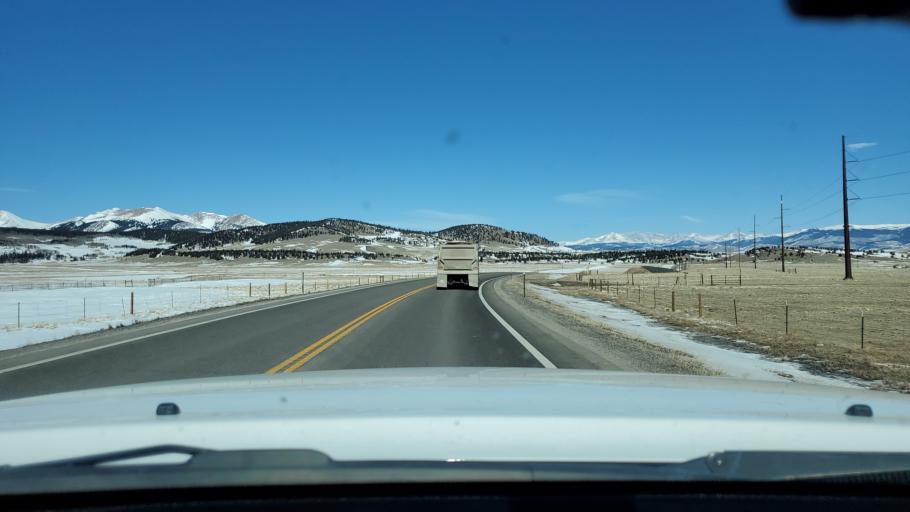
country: US
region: Colorado
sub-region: Park County
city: Fairplay
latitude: 39.2833
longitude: -105.9136
